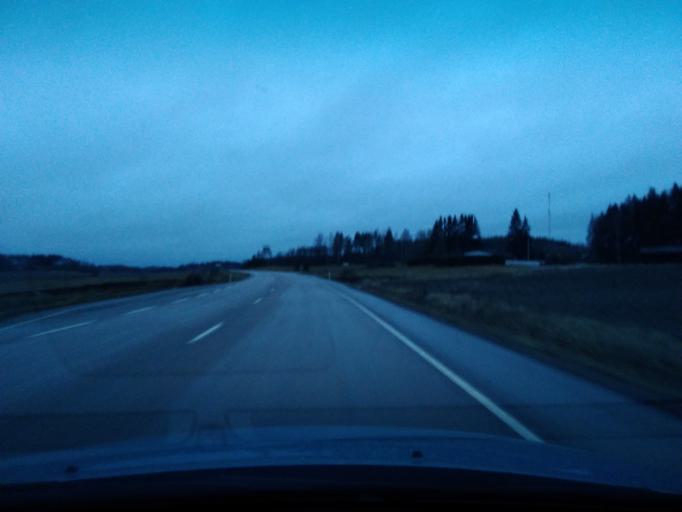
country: FI
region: Uusimaa
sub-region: Porvoo
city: Askola
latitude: 60.4750
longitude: 25.5686
